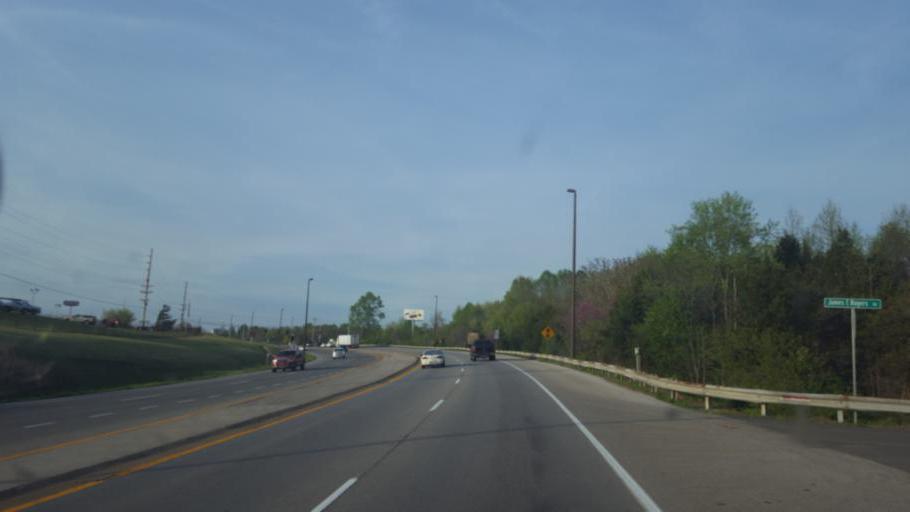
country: US
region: Kentucky
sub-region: Barren County
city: Glasgow
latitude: 36.9804
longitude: -85.9323
